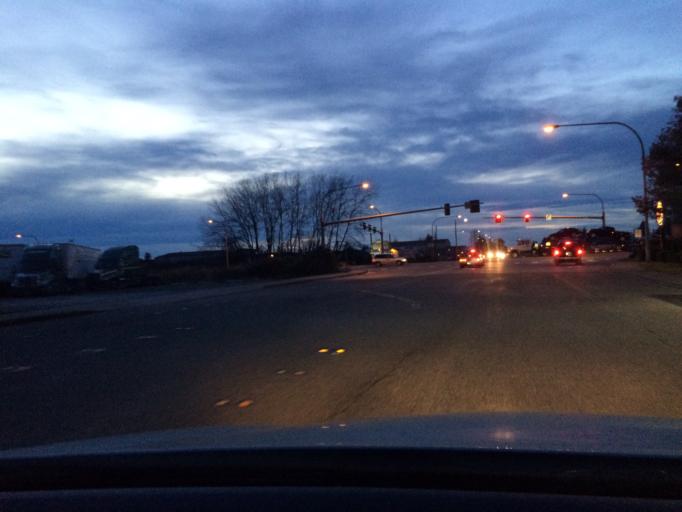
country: US
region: Washington
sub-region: Whatcom County
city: Blaine
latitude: 48.9941
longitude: -122.7337
